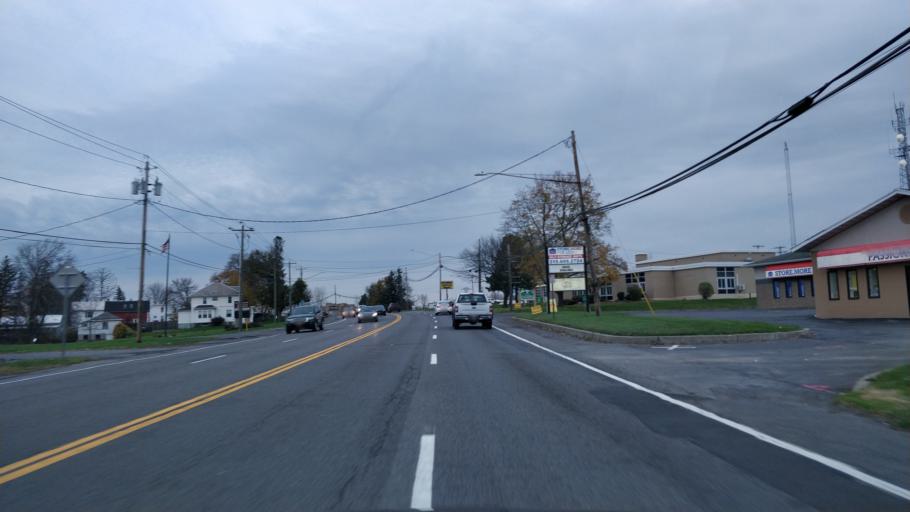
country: US
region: New York
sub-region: Onondaga County
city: North Syracuse
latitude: 43.1682
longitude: -76.1175
